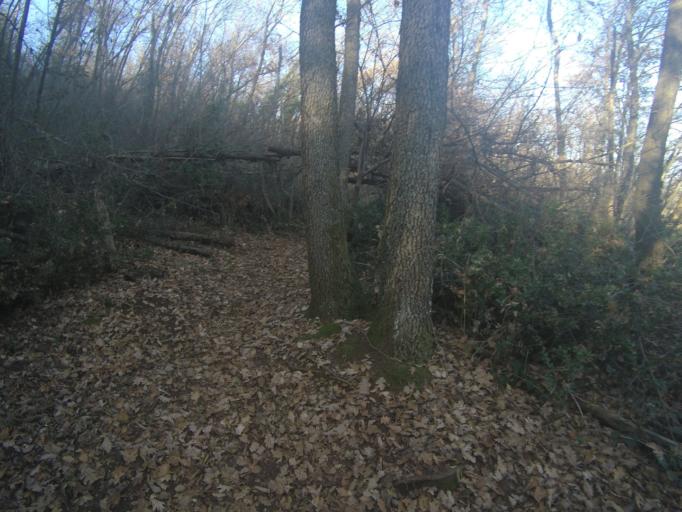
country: IT
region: Veneto
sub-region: Provincia di Vicenza
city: Lumignano
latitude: 45.4501
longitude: 11.5778
